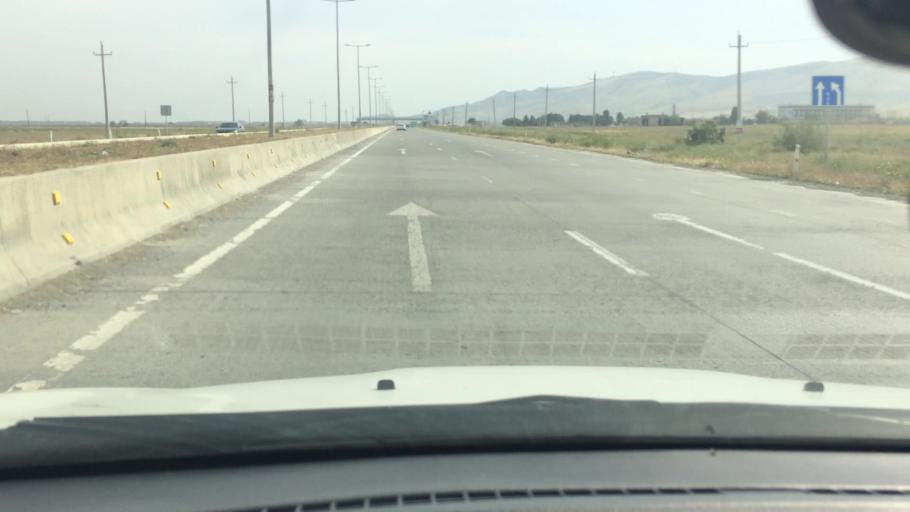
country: GE
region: Kvemo Kartli
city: Rust'avi
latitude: 41.5988
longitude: 44.9416
